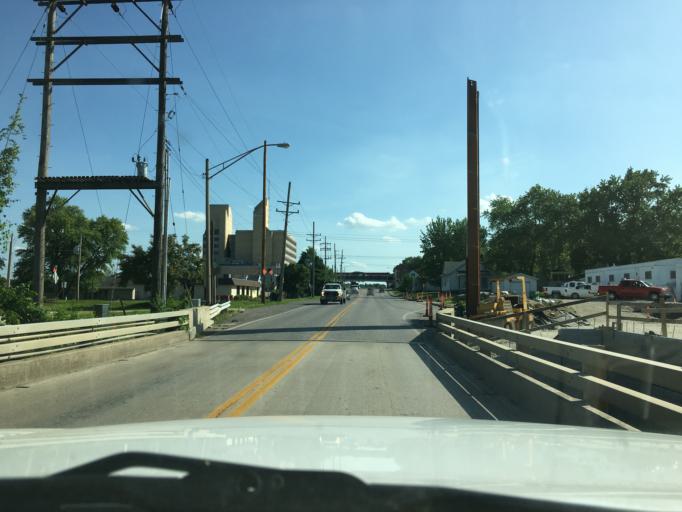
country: US
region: Missouri
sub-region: Franklin County
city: Washington
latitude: 38.5552
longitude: -90.9999
